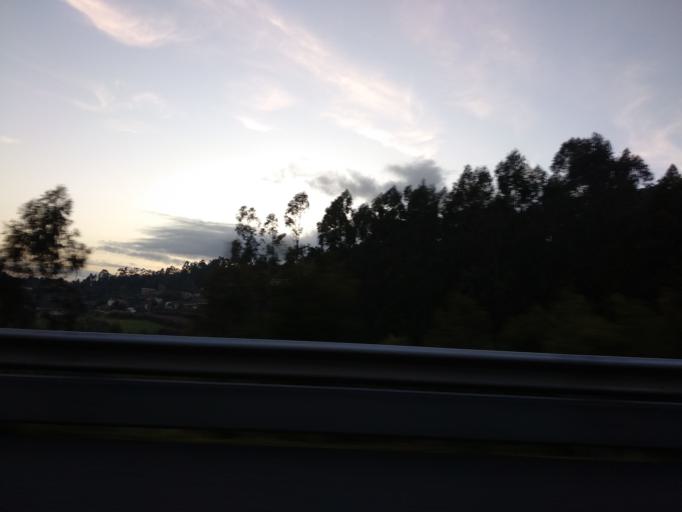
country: PT
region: Braga
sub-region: Vila Nova de Famalicao
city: Vila Nova de Famalicao
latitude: 41.4331
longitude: -8.4976
